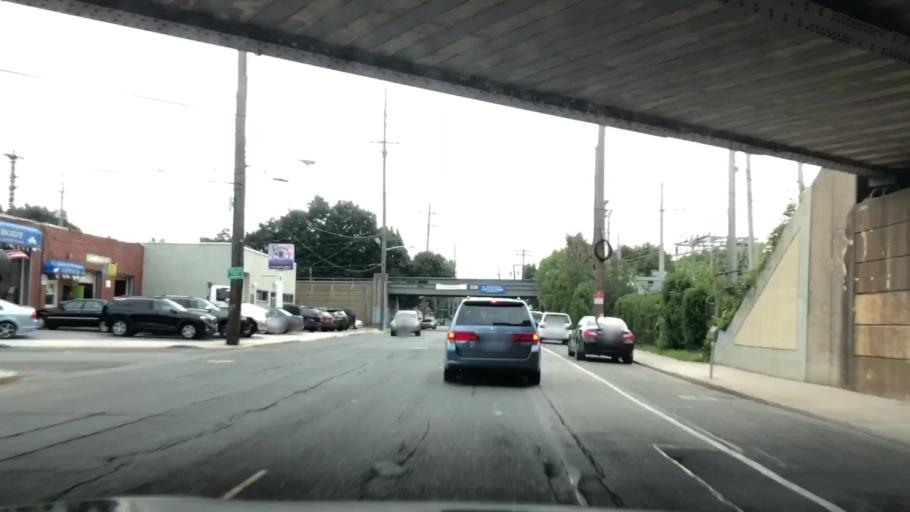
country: US
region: New York
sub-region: Nassau County
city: Floral Park
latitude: 40.7259
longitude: -73.7014
